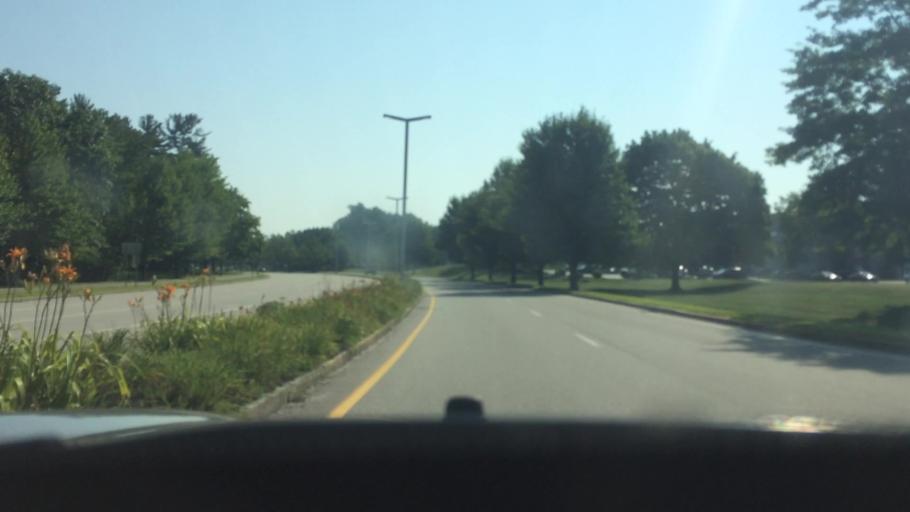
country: US
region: Maine
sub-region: York County
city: South Eliot
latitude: 43.0881
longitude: -70.8083
